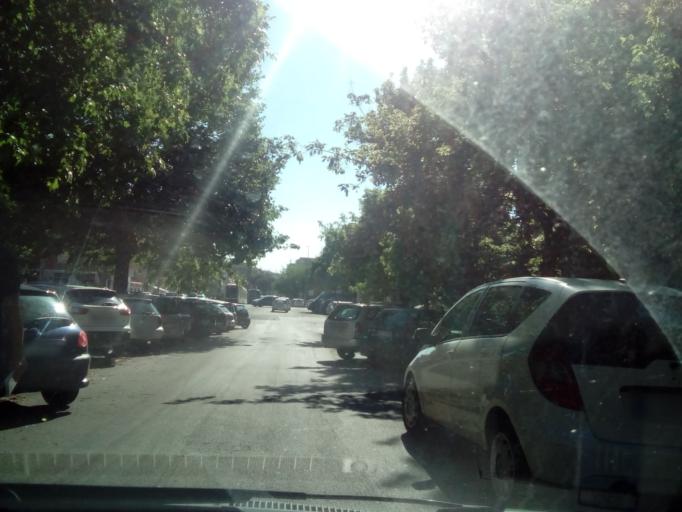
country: IT
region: Latium
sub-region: Citta metropolitana di Roma Capitale
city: Rome
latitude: 41.8917
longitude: 12.5652
